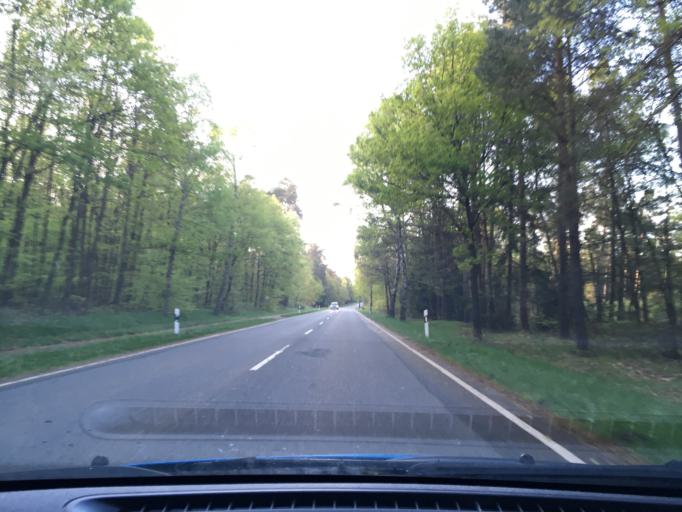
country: DE
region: Lower Saxony
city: Bispingen
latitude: 53.0344
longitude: 9.9979
